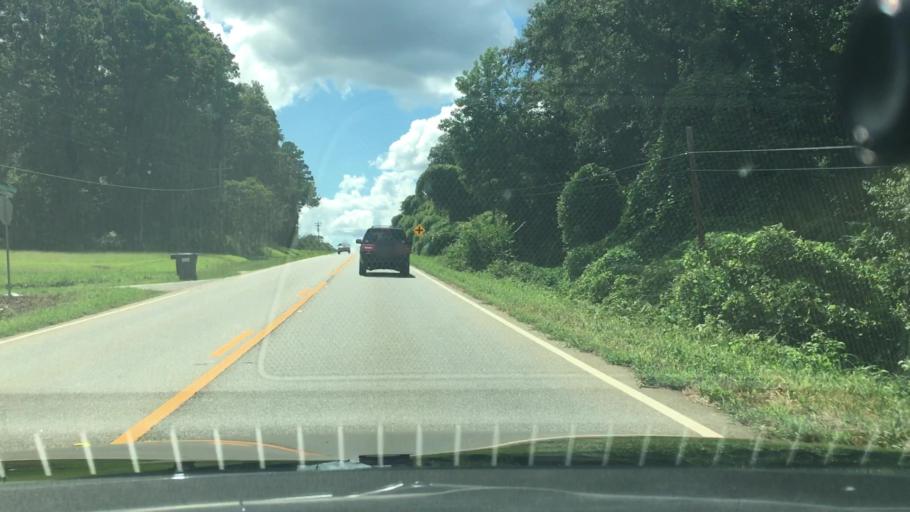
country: US
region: Georgia
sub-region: Putnam County
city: Eatonton
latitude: 33.3187
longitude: -83.4149
